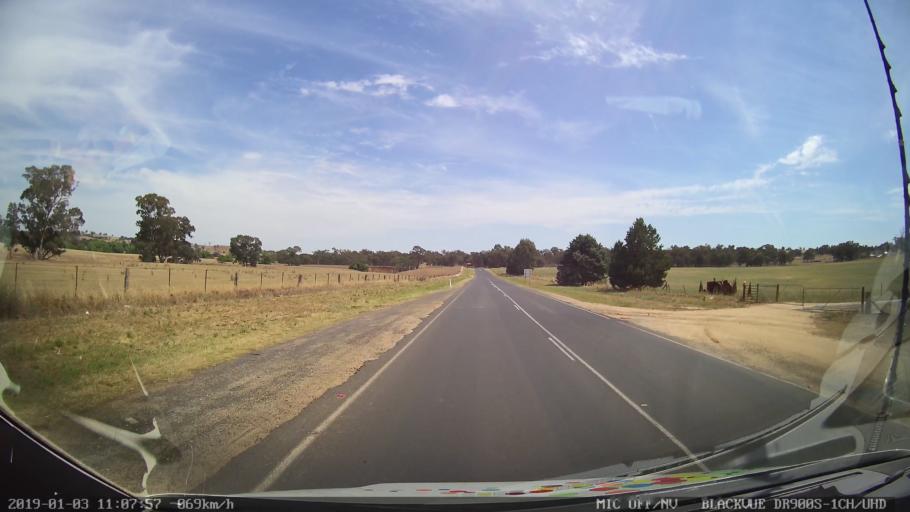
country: AU
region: New South Wales
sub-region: Young
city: Young
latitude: -34.2545
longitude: 148.2588
